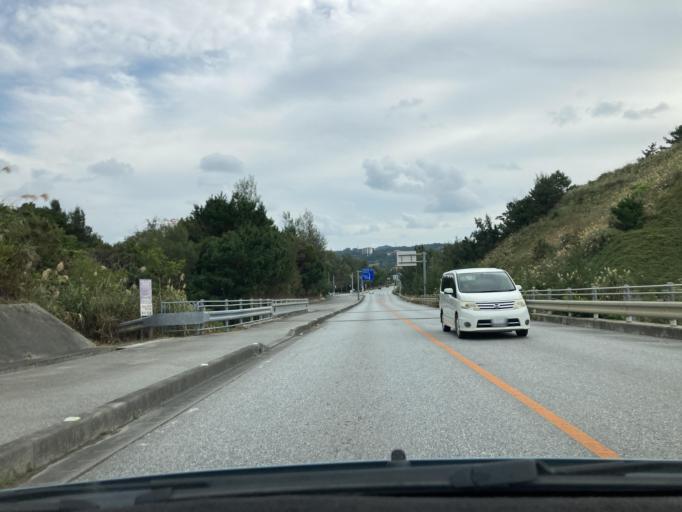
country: JP
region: Okinawa
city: Ishikawa
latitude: 26.5040
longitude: 127.8775
